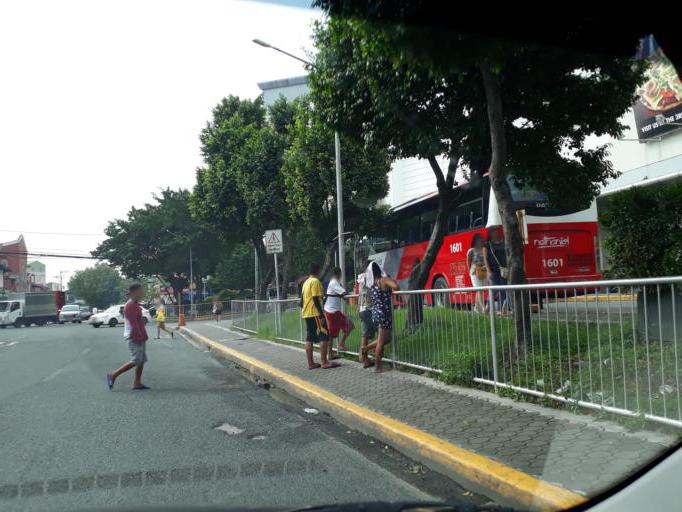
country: PH
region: Metro Manila
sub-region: City of Manila
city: Manila
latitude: 14.6178
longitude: 120.9851
